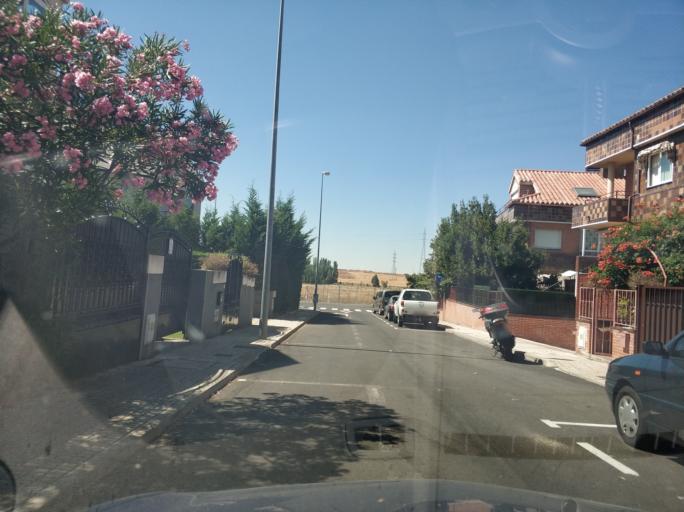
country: ES
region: Castille and Leon
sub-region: Provincia de Salamanca
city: Villares de la Reina
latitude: 40.9951
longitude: -5.6566
